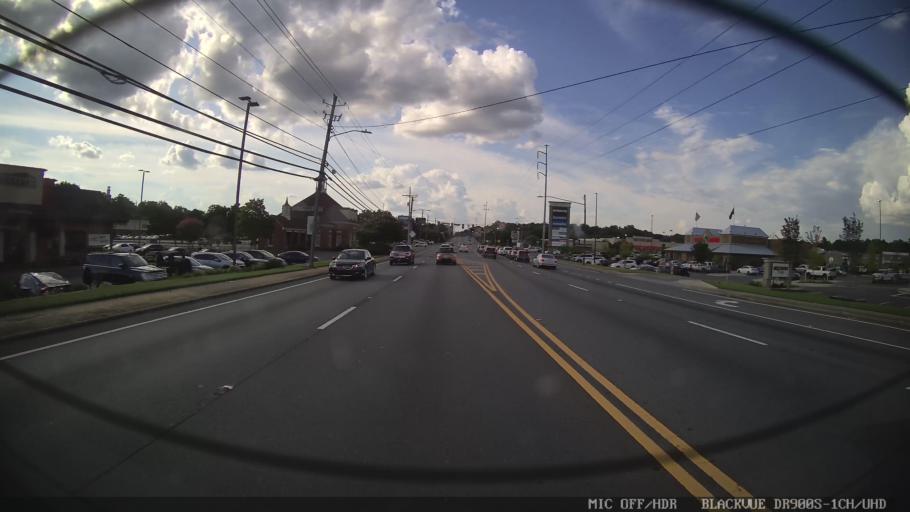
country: US
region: Georgia
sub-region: Floyd County
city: Rome
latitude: 34.2513
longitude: -85.1632
